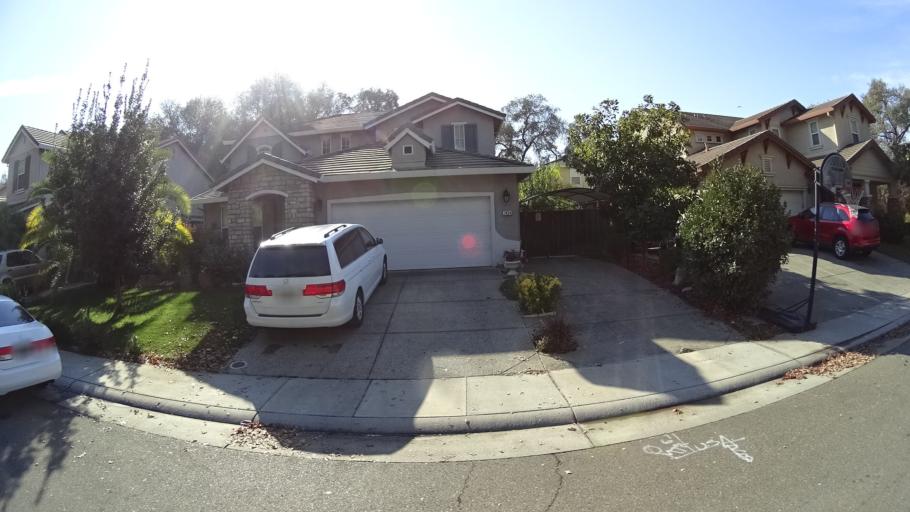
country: US
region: California
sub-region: Sacramento County
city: Citrus Heights
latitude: 38.6876
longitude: -121.2945
